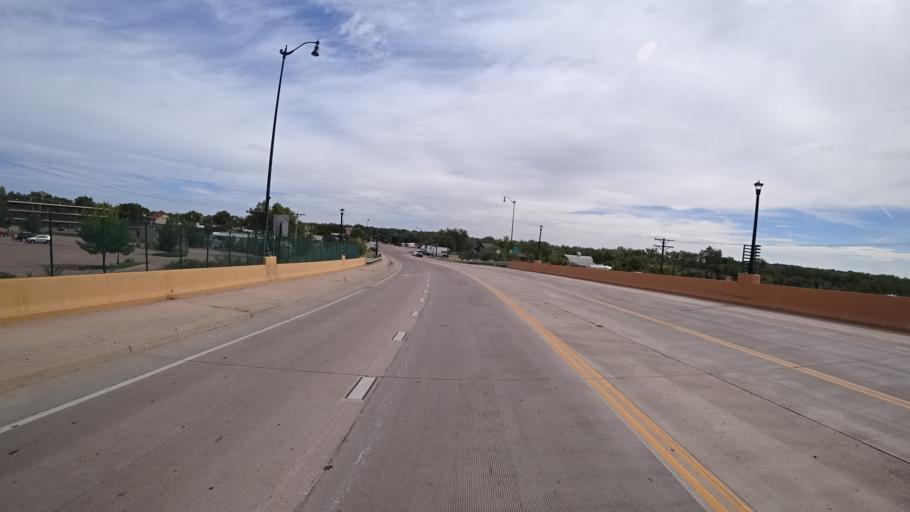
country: US
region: Colorado
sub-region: El Paso County
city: Fountain
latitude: 38.6743
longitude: -104.7068
